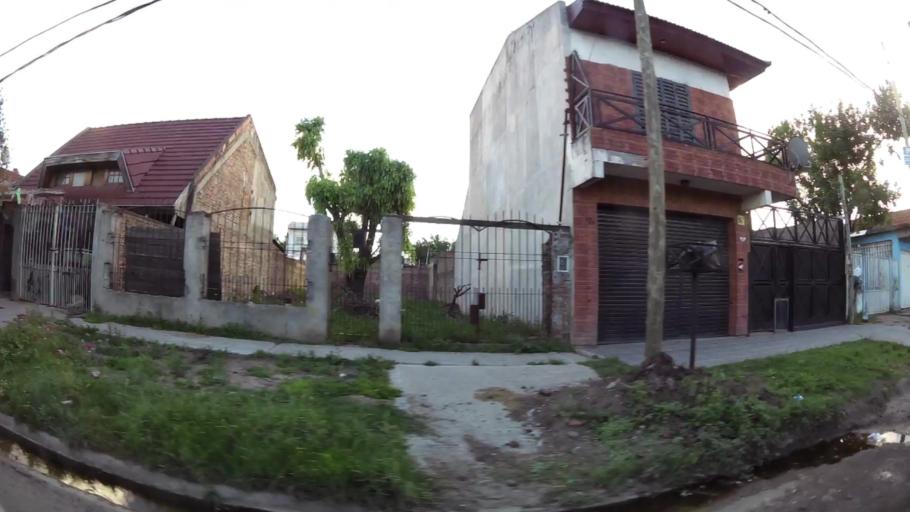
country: AR
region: Buenos Aires
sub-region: Partido de Moron
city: Moron
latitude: -34.7078
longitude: -58.6171
